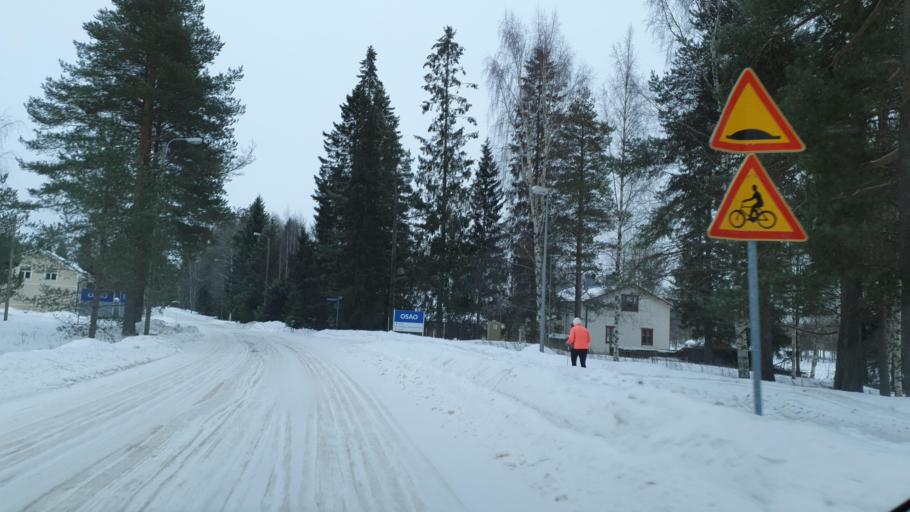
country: FI
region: Northern Ostrobothnia
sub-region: Oulu
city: Haukipudas
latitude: 65.1939
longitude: 25.4118
